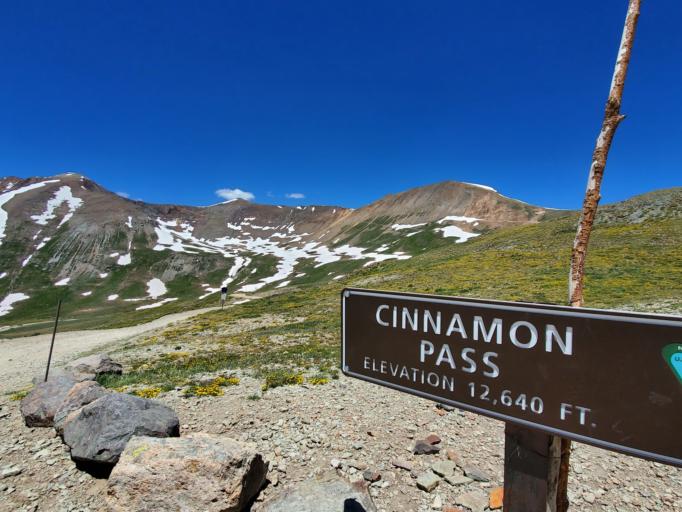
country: US
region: Colorado
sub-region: Ouray County
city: Ouray
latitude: 37.9337
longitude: -107.5382
